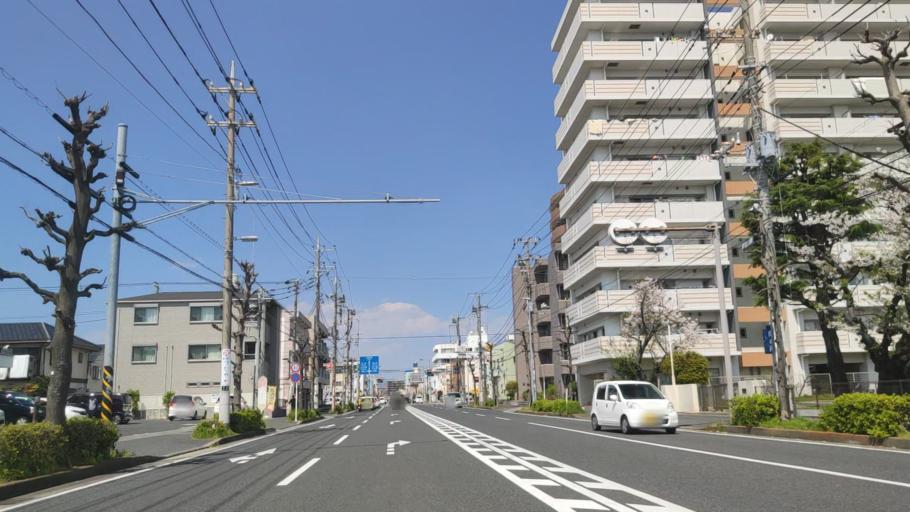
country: JP
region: Kanagawa
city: Hiratsuka
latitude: 35.3304
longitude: 139.3402
